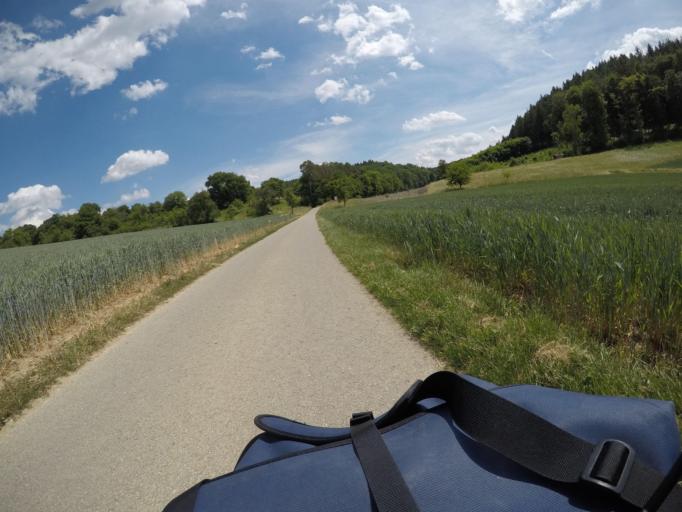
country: DE
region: Baden-Wuerttemberg
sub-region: Regierungsbezirk Stuttgart
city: Ittlingen
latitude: 49.2156
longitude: 8.9360
